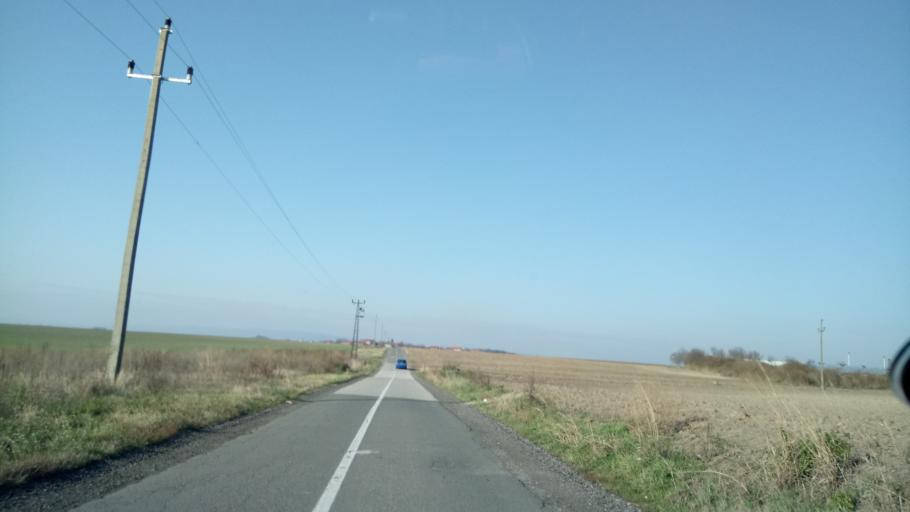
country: RS
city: Ljukovo
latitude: 45.0370
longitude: 20.0412
